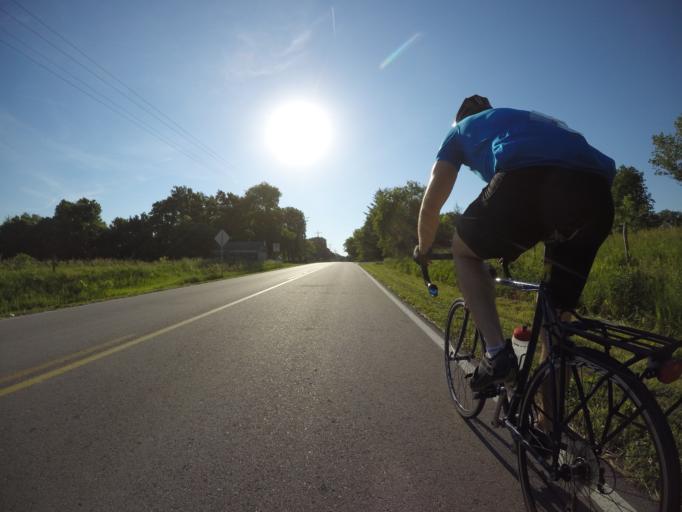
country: US
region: Nebraska
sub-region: Gage County
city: Wymore
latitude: 40.0883
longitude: -96.4862
